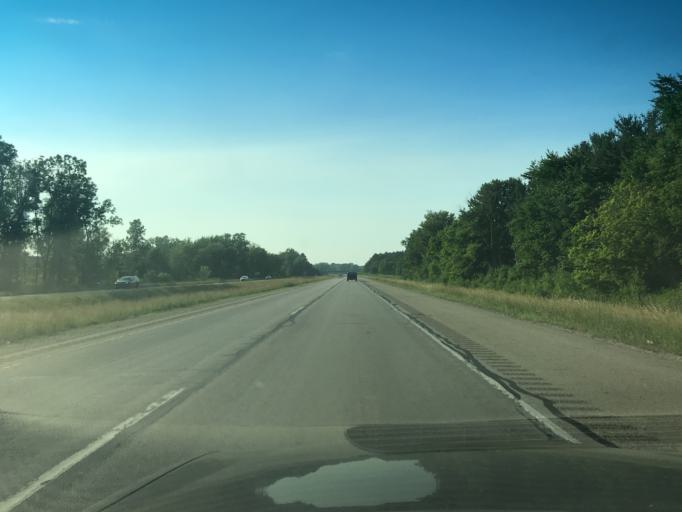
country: US
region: Michigan
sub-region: Ingham County
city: Mason
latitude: 42.6045
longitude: -84.4698
